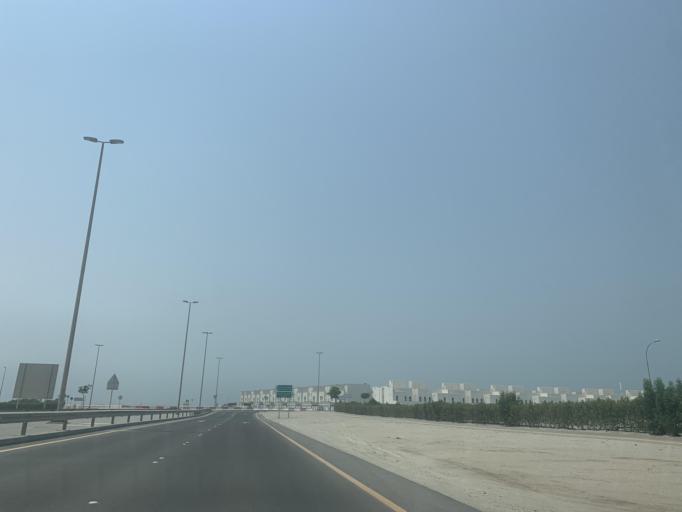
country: BH
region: Muharraq
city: Al Muharraq
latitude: 26.3117
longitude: 50.6218
